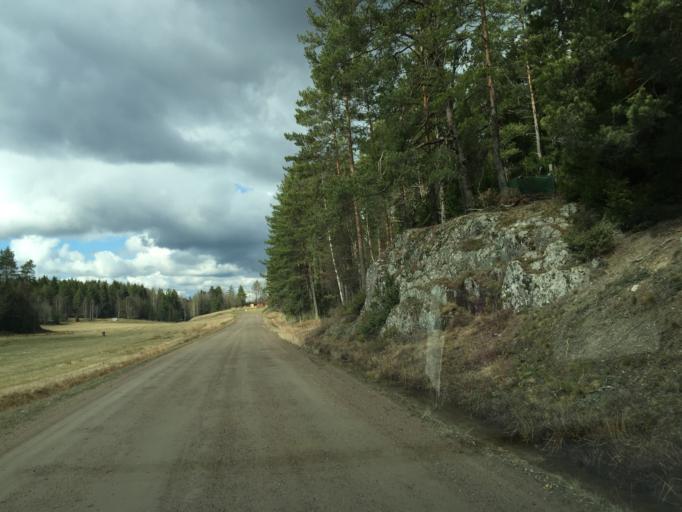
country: SE
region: Soedermanland
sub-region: Nykopings Kommun
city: Nykoping
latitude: 58.9581
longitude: 17.0525
